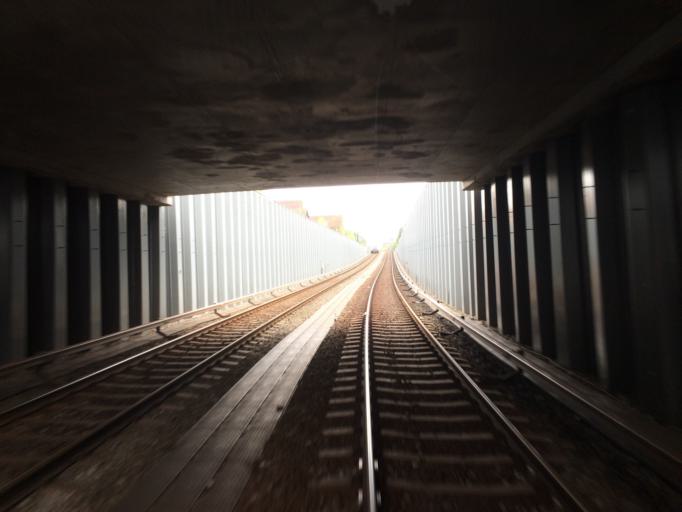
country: DK
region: Capital Region
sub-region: Tarnby Kommune
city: Tarnby
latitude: 55.6392
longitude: 12.6449
